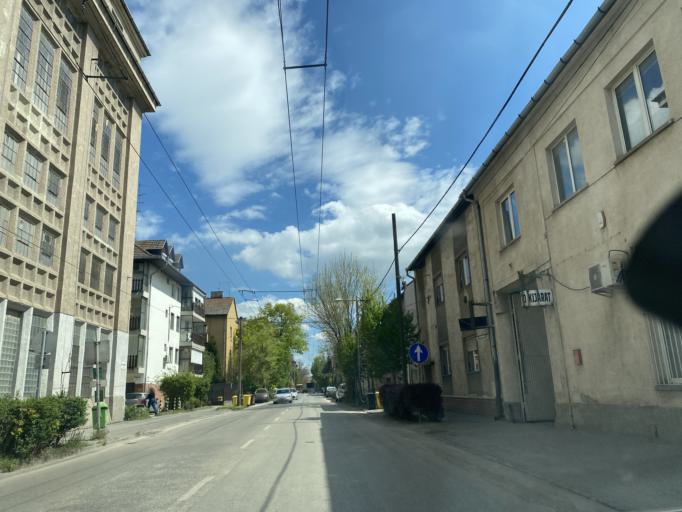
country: HU
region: Csongrad
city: Szeged
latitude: 46.2564
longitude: 20.1347
